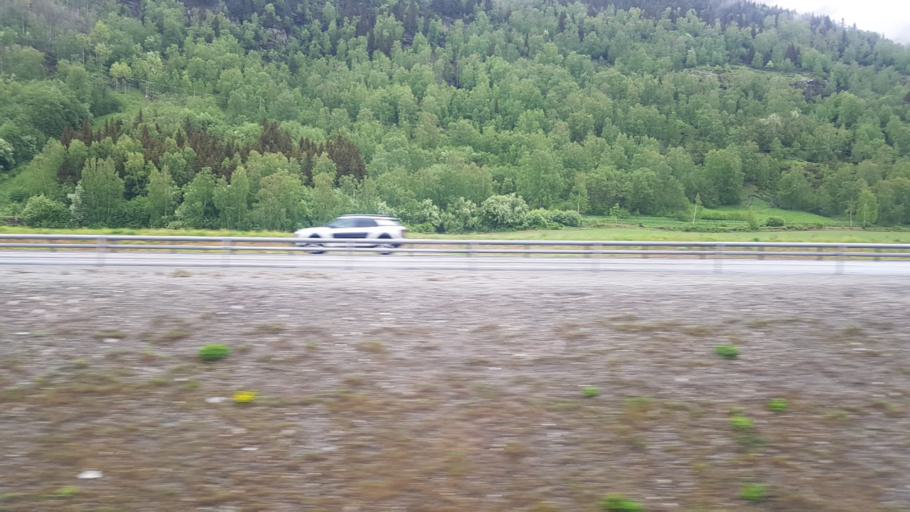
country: NO
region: Oppland
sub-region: Sor-Fron
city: Hundorp
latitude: 61.5472
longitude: 10.0286
